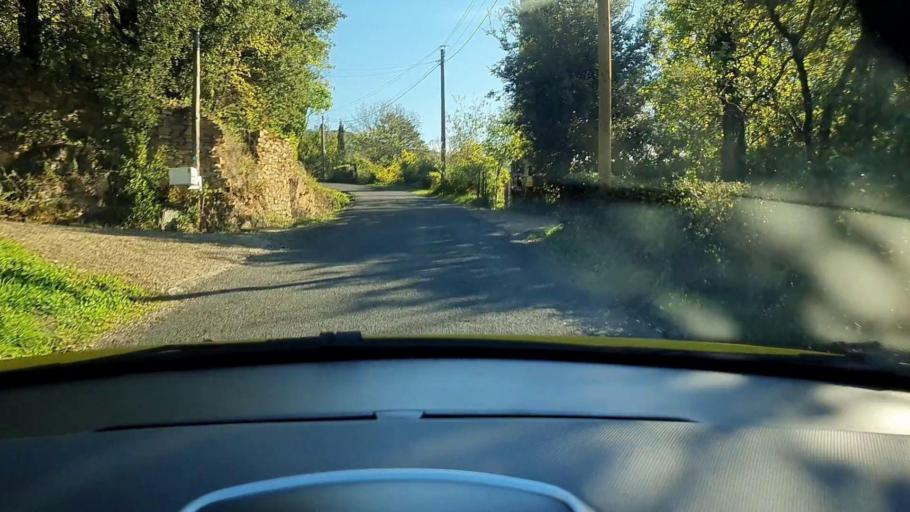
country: FR
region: Languedoc-Roussillon
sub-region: Departement du Gard
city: Le Vigan
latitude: 43.9953
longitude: 3.6251
